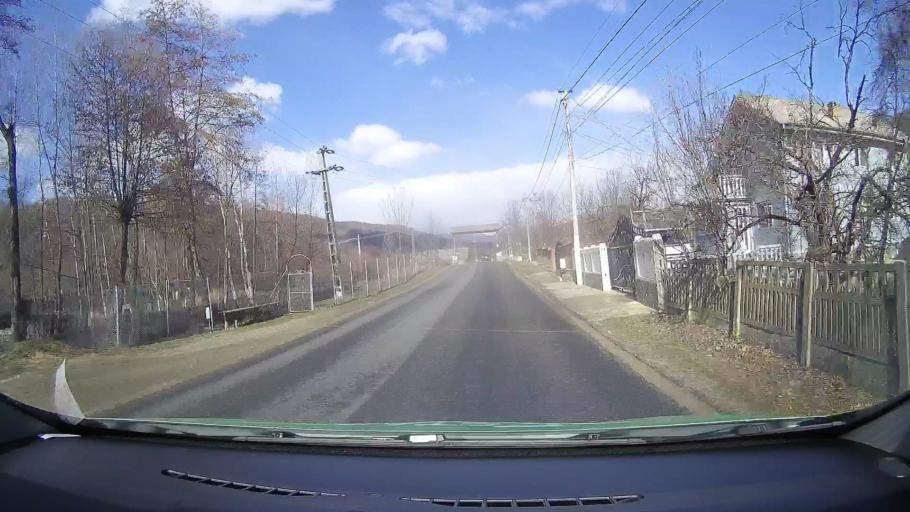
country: RO
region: Dambovita
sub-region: Comuna Runcu
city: Badeni
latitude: 45.1496
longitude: 25.4026
